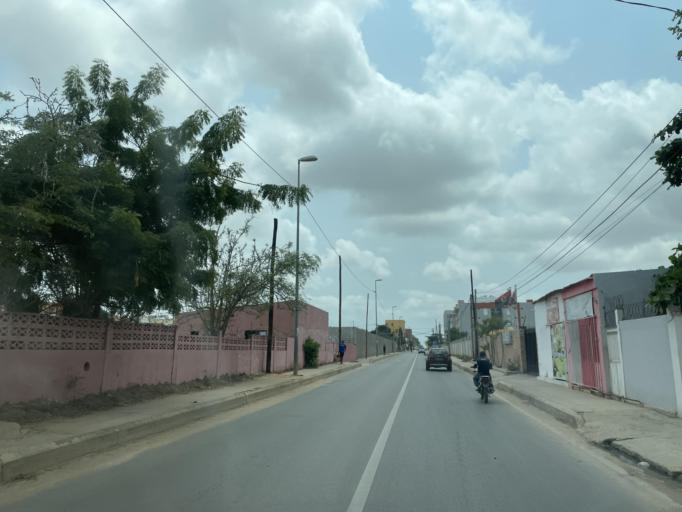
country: AO
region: Luanda
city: Luanda
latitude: -8.9405
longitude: 13.1665
